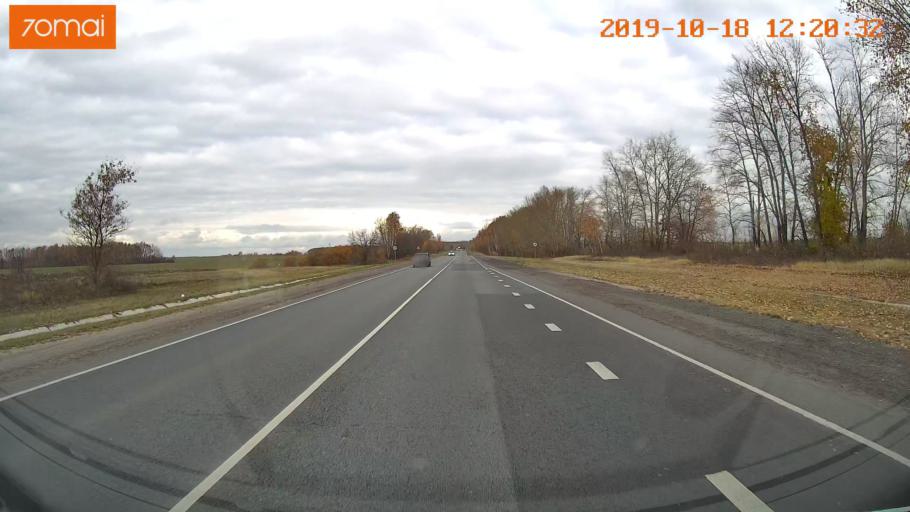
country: RU
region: Rjazan
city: Bagramovo
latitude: 54.4992
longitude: 39.4815
